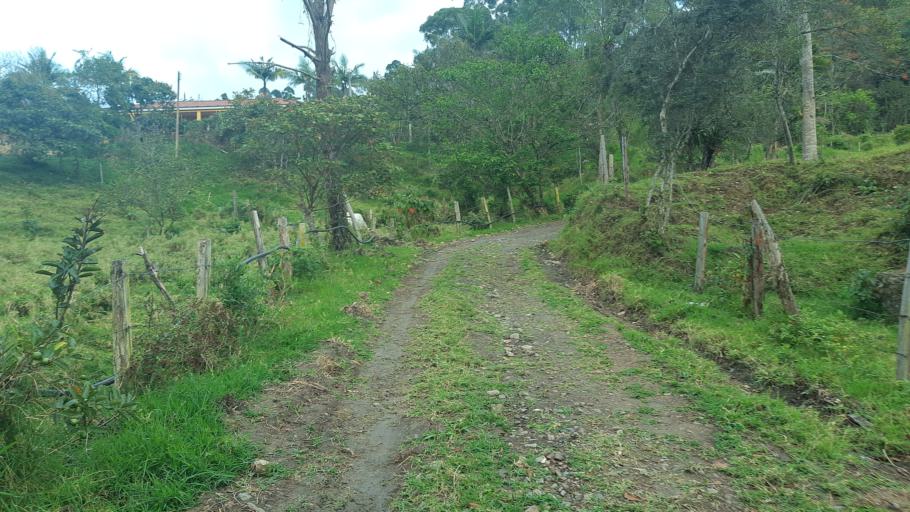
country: CO
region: Boyaca
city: Garagoa
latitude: 5.0792
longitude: -73.3734
